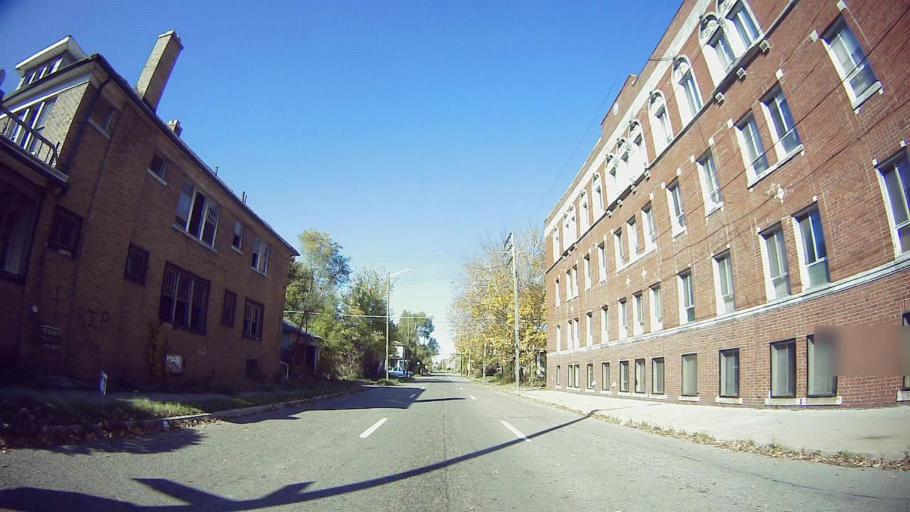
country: US
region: Michigan
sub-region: Wayne County
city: Highland Park
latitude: 42.3870
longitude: -83.1096
